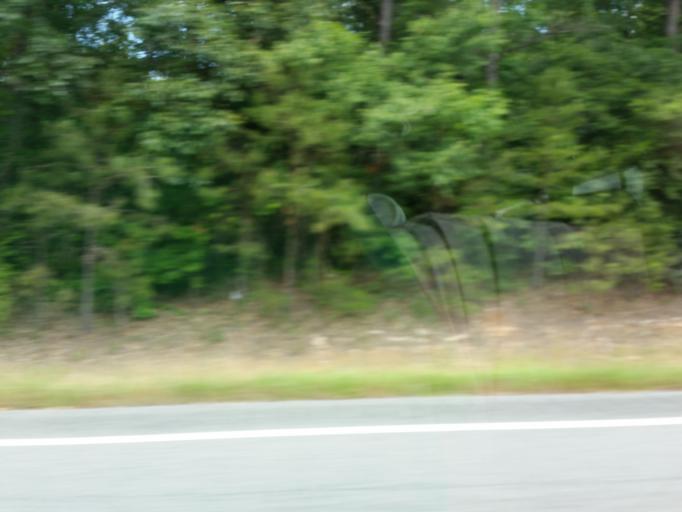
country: US
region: Alabama
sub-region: Sumter County
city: York
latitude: 32.3710
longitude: -88.1927
